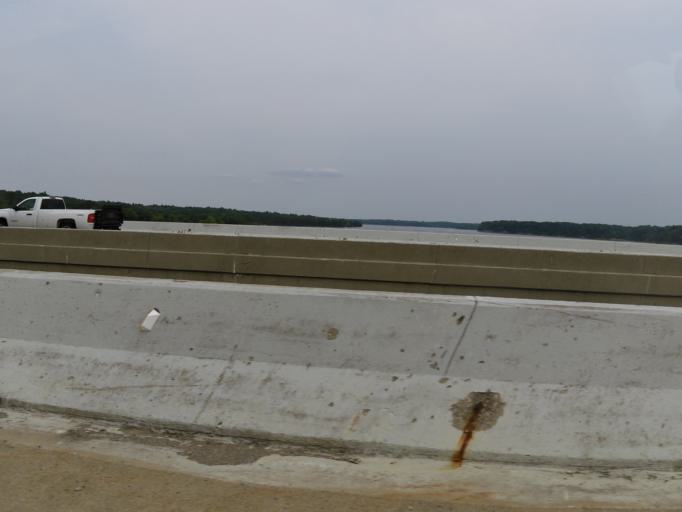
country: US
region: Ohio
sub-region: Warren County
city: Waynesville
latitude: 39.5072
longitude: -84.0240
